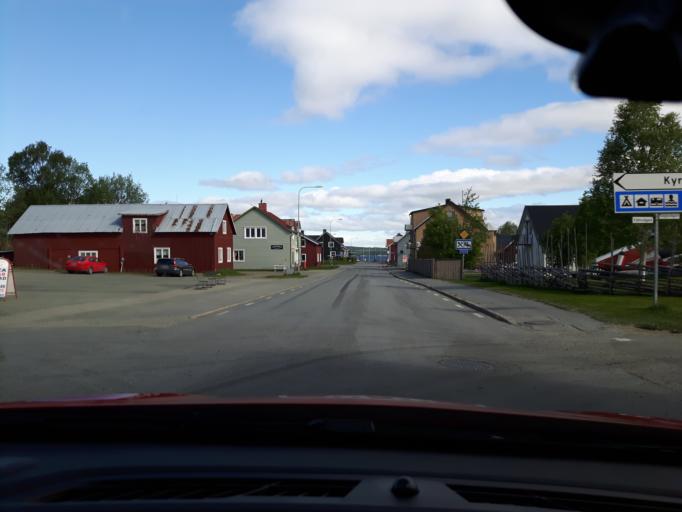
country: NO
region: Nord-Trondelag
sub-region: Lierne
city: Sandvika
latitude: 64.5044
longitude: 14.1461
